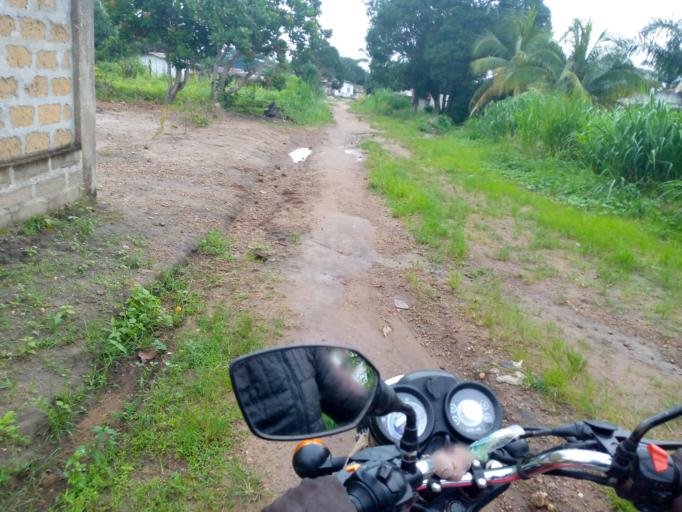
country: SL
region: Eastern Province
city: Kenema
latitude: 7.8459
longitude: -11.2064
